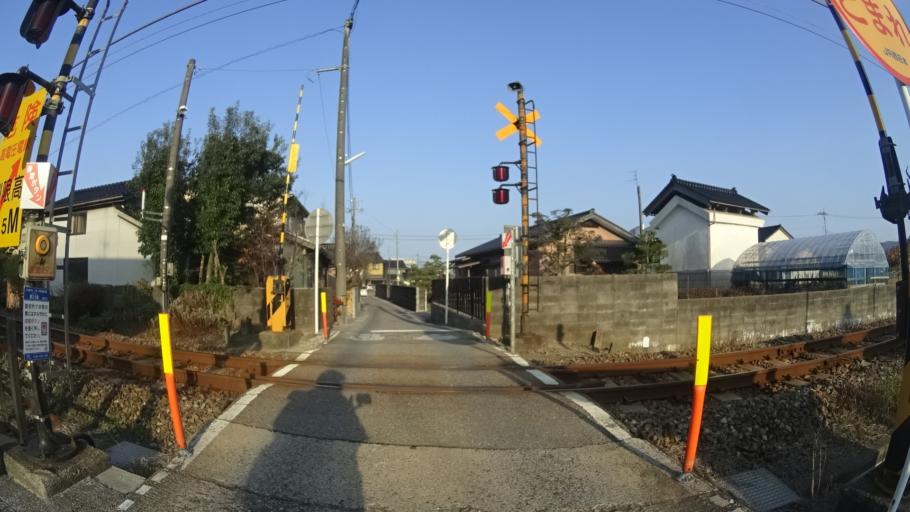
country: JP
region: Ishikawa
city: Nanao
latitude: 37.0505
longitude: 136.9557
